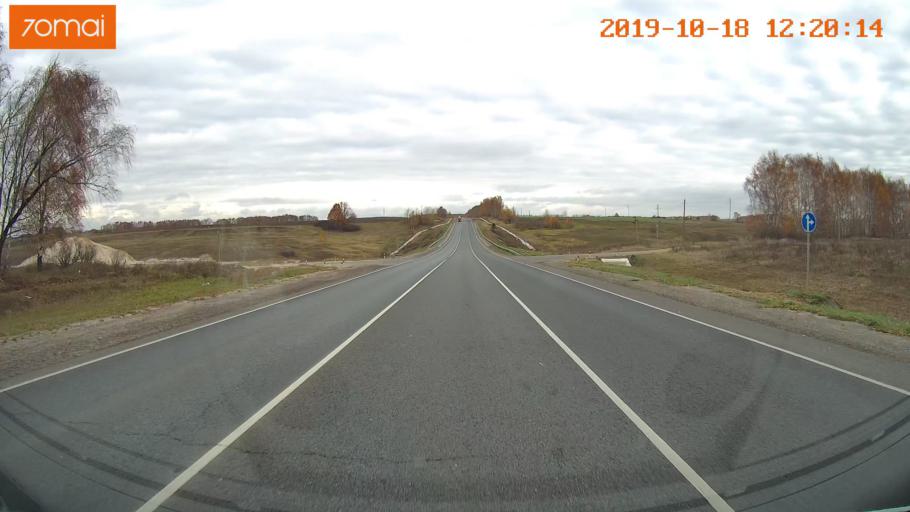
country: RU
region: Rjazan
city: Bagramovo
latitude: 54.4945
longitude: 39.4777
